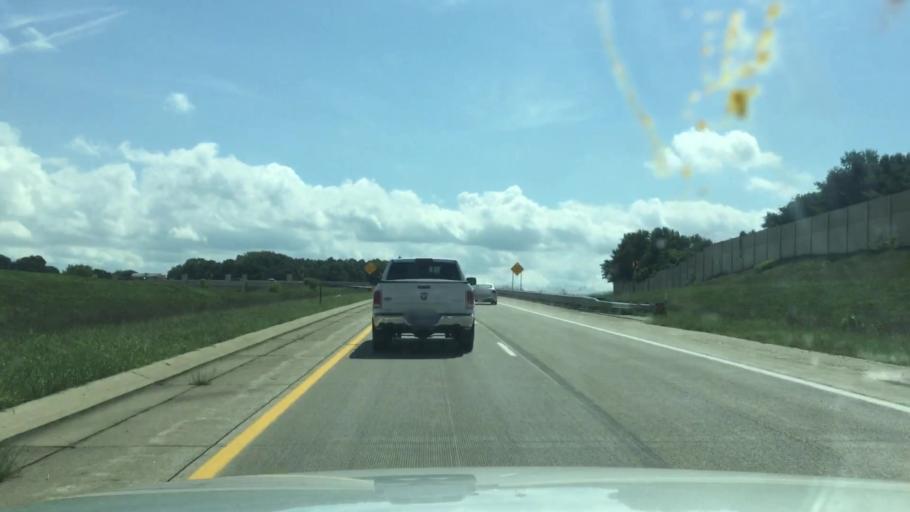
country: US
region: Michigan
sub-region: Kalamazoo County
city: Westwood
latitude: 42.2375
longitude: -85.6406
